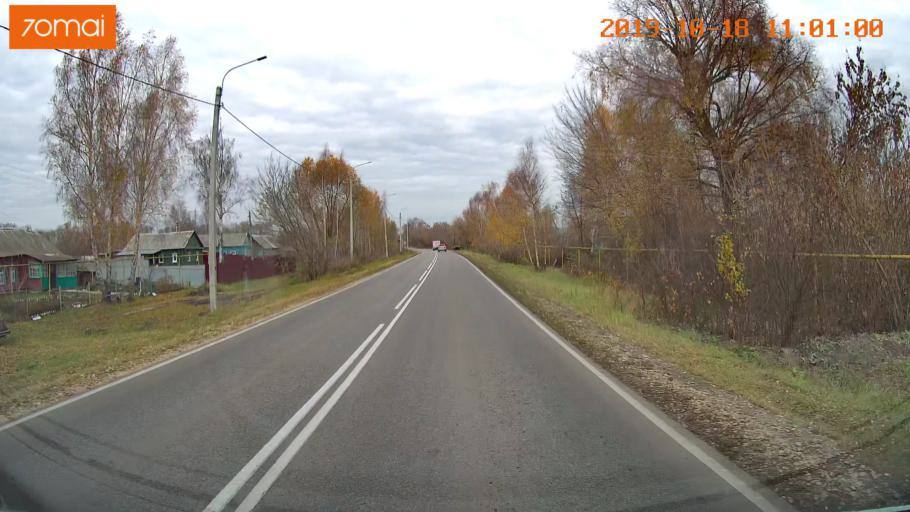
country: RU
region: Tula
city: Yepifan'
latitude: 53.8496
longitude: 38.5527
